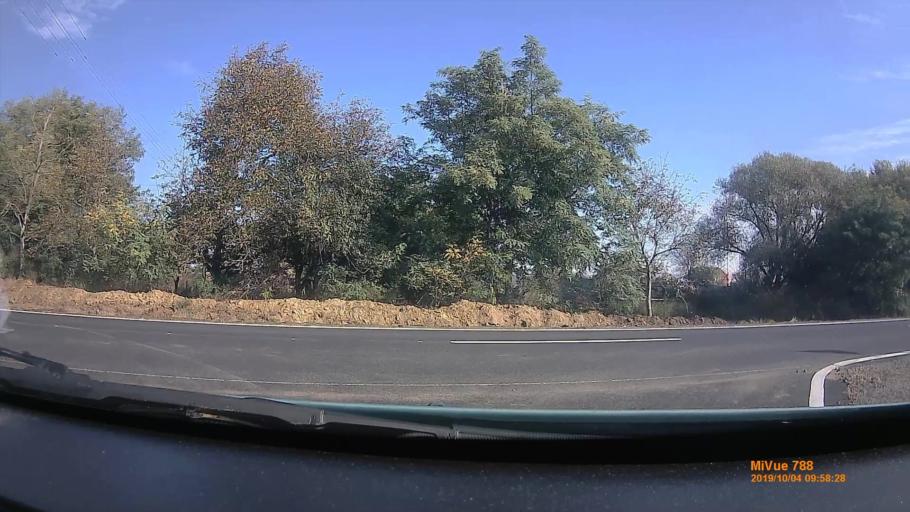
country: HU
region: Szabolcs-Szatmar-Bereg
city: Nyiregyhaza
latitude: 47.9421
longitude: 21.6641
